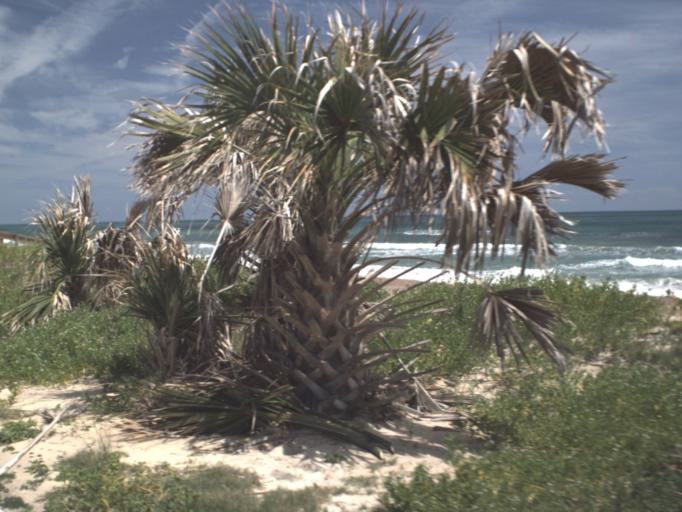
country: US
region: Florida
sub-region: Flagler County
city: Flagler Beach
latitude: 29.4298
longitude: -81.1038
